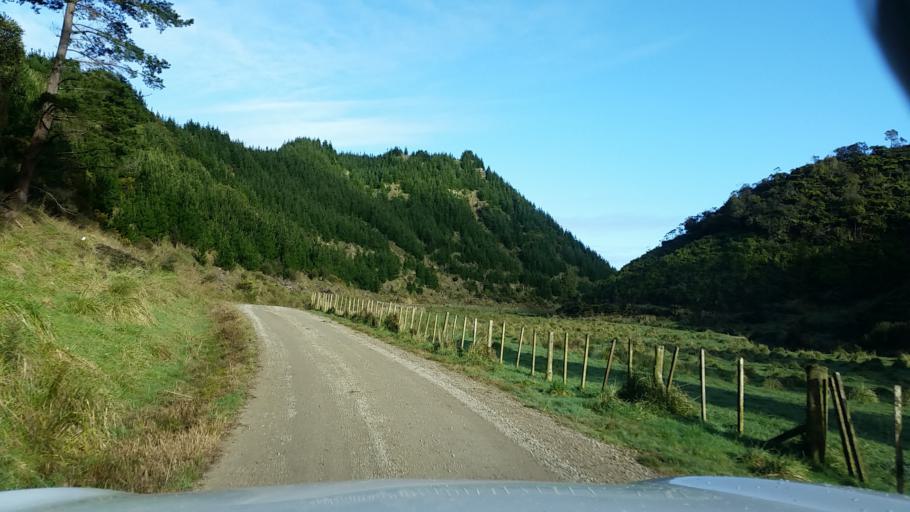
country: NZ
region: Taranaki
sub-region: South Taranaki District
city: Patea
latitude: -39.6913
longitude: 174.7595
